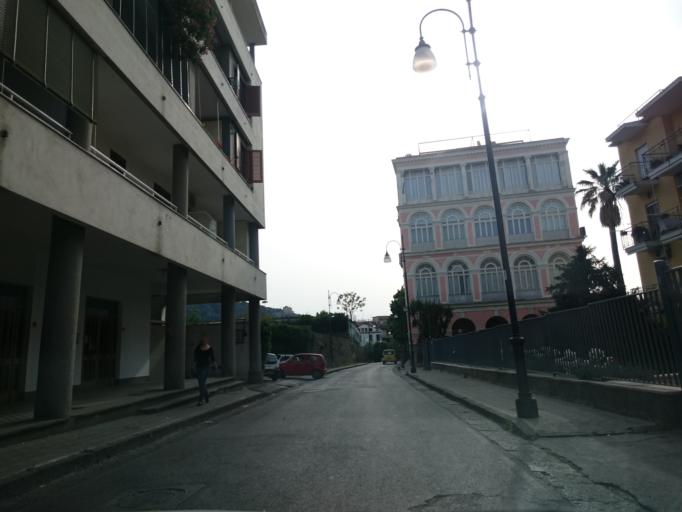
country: IT
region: Campania
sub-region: Provincia di Napoli
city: Sant'Agnello
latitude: 40.6313
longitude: 14.4040
